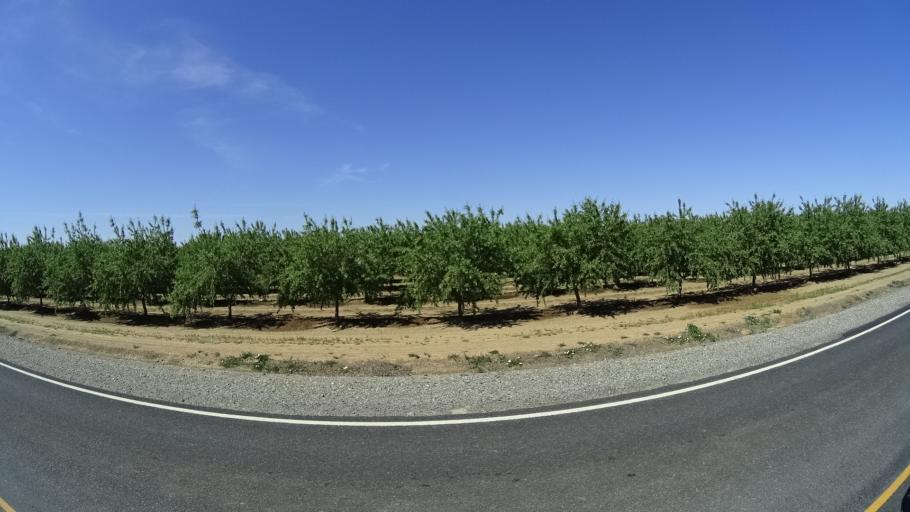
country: US
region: California
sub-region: Glenn County
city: Orland
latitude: 39.6370
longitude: -122.1411
